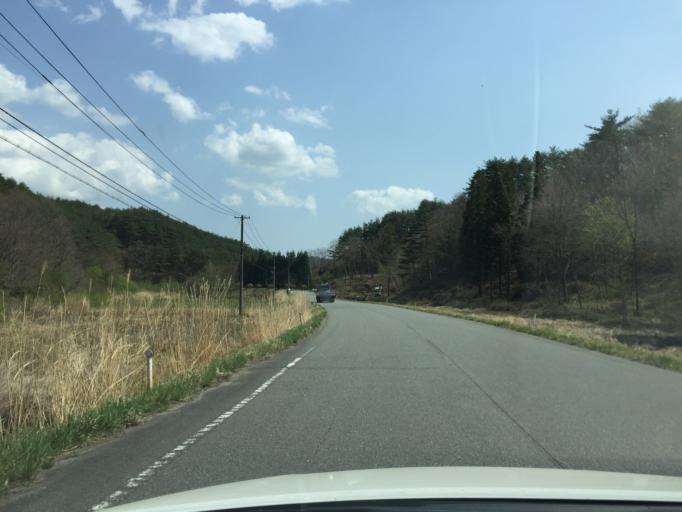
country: JP
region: Fukushima
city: Namie
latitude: 37.3689
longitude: 140.8072
